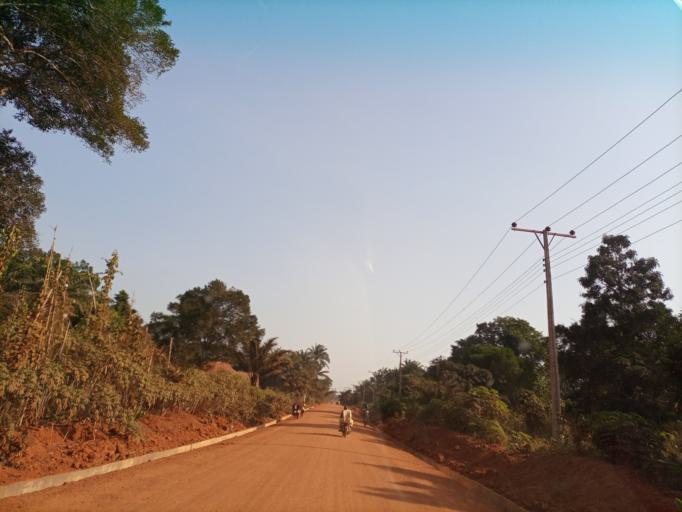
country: NG
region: Enugu
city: Opi
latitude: 6.7516
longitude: 7.4083
